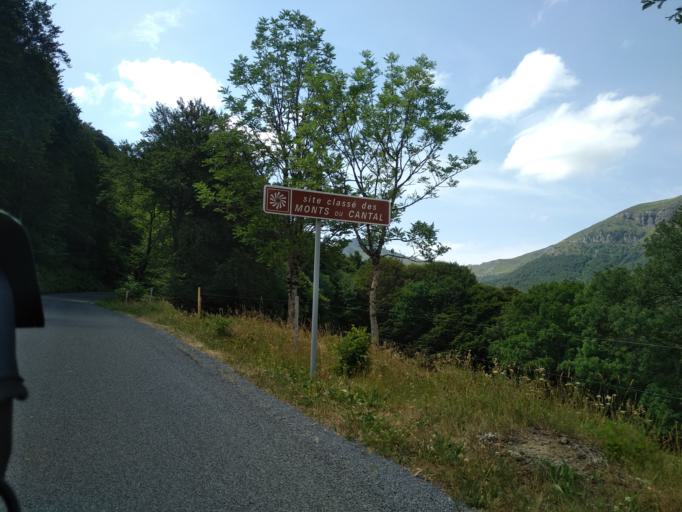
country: FR
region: Auvergne
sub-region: Departement du Cantal
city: Riom-es-Montagnes
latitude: 45.1333
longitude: 2.6985
